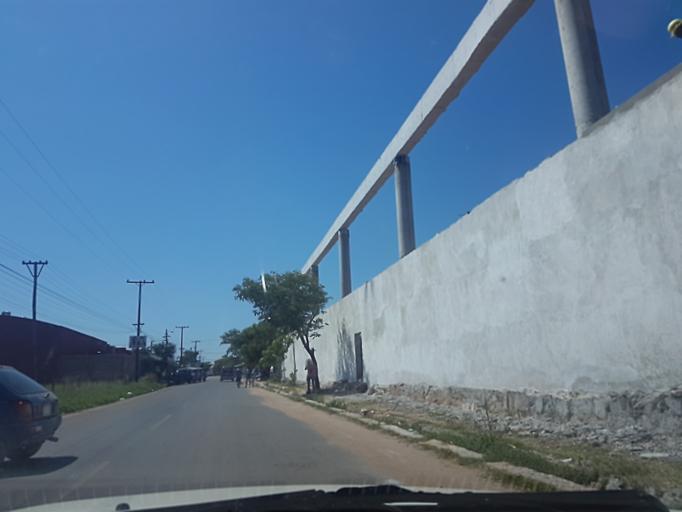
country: PY
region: Central
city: Limpio
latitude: -25.1759
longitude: -57.4829
